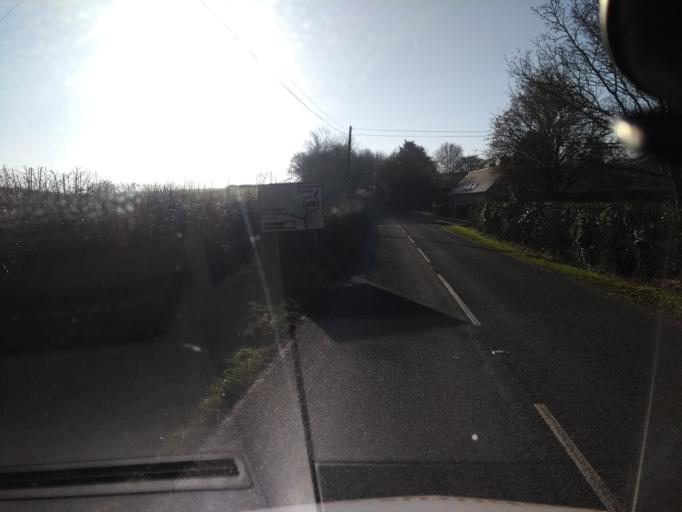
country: GB
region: England
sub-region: Somerset
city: Redlynch
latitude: 51.0883
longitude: -2.4144
